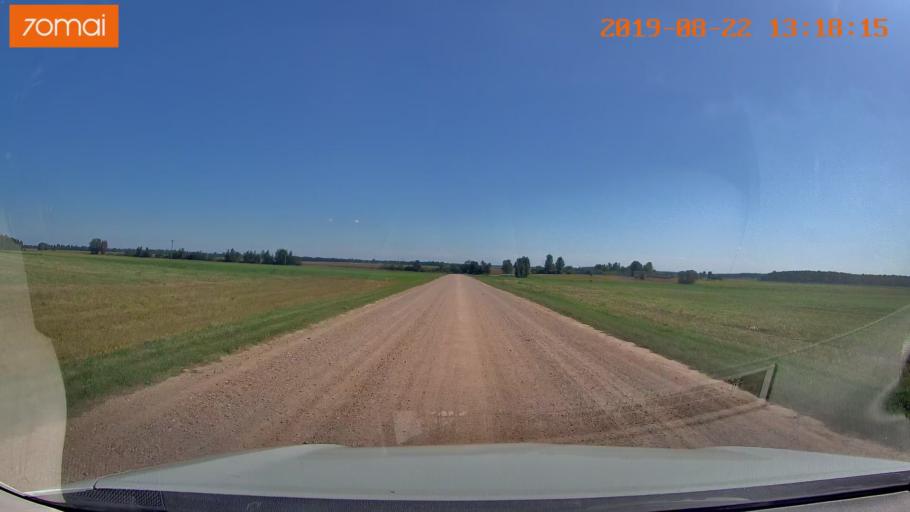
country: BY
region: Minsk
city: Urechcha
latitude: 53.2421
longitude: 27.9355
